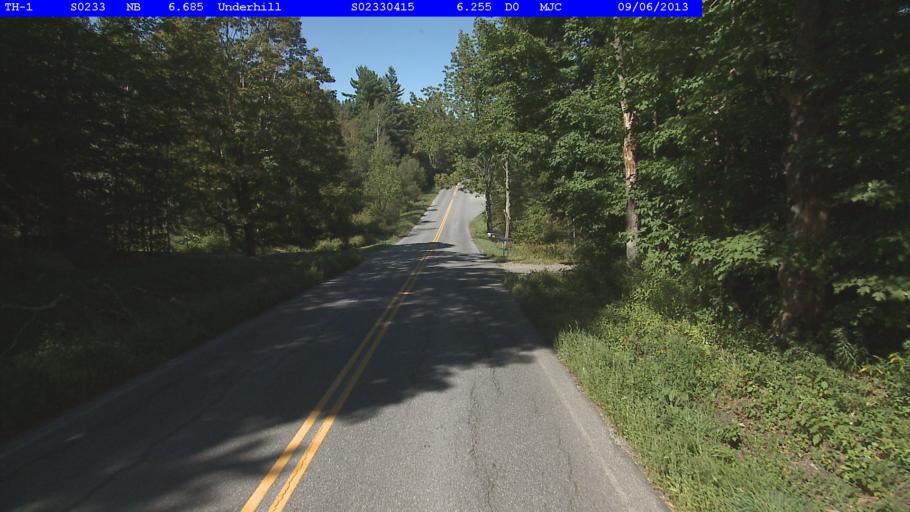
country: US
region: Vermont
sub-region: Chittenden County
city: Jericho
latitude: 44.5551
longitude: -72.8673
